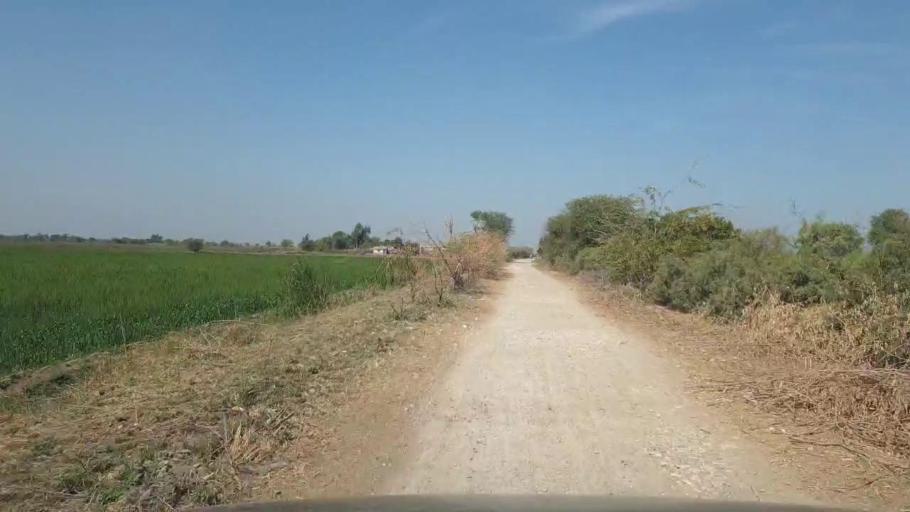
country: PK
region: Sindh
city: Mirpur Khas
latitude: 25.4398
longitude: 69.1644
